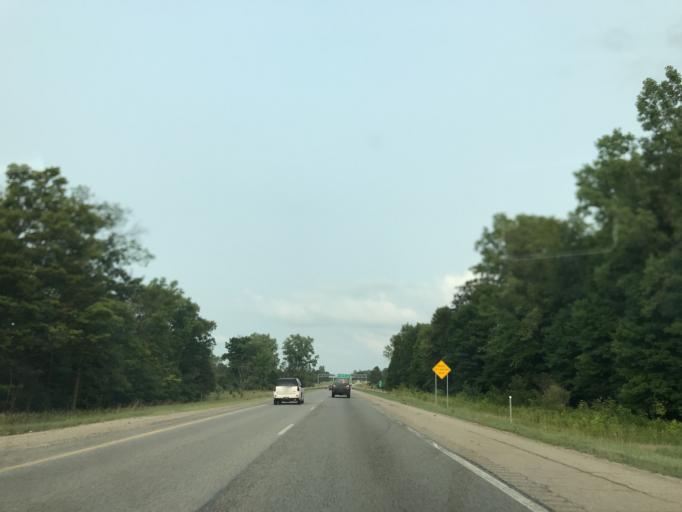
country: US
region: Michigan
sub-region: Ingham County
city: Williamston
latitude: 42.6654
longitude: -84.2935
